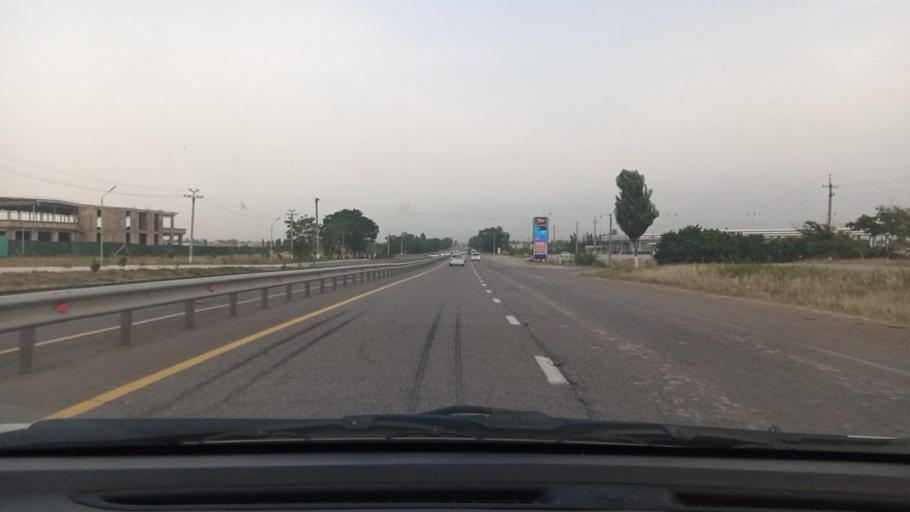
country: UZ
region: Toshkent
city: Ohangaron
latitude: 40.9407
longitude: 69.5822
